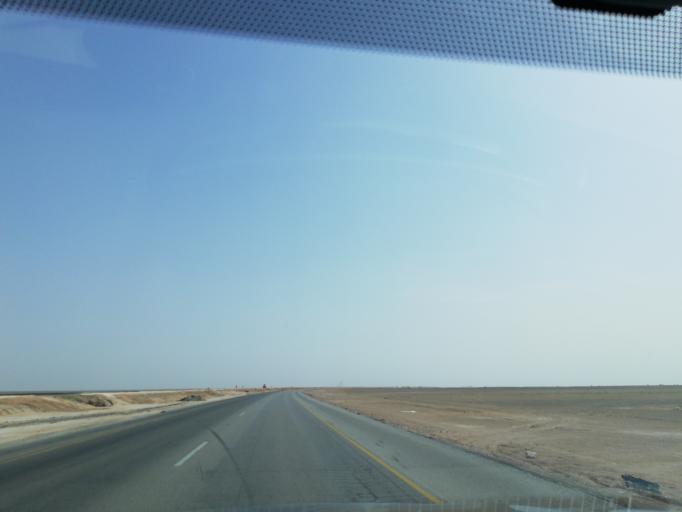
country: OM
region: Muhafazat ad Dakhiliyah
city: Adam
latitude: 21.6897
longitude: 57.3260
